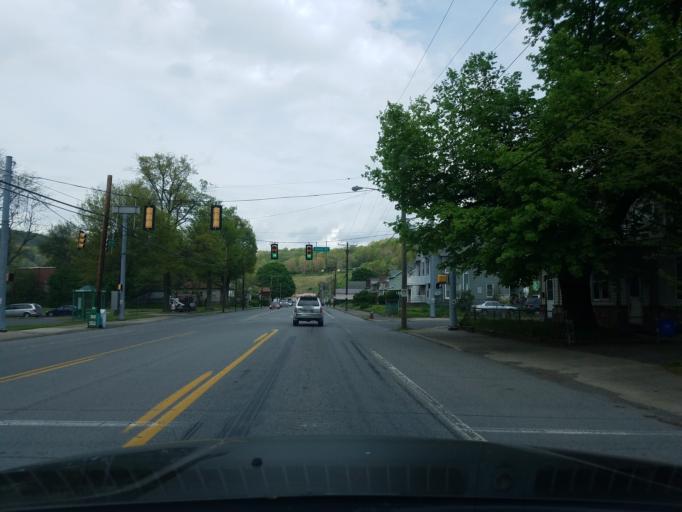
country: US
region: Pennsylvania
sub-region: Cambria County
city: Johnstown
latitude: 40.3553
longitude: -78.9371
